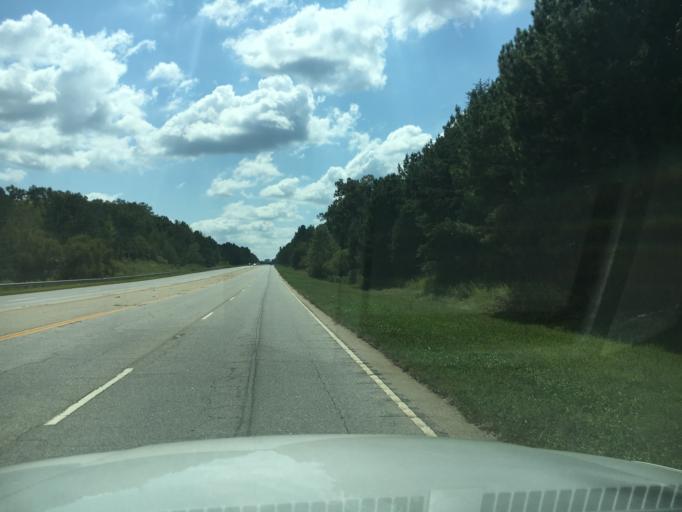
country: US
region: South Carolina
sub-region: Greenwood County
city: Ware Shoals
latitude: 34.3901
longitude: -82.2238
